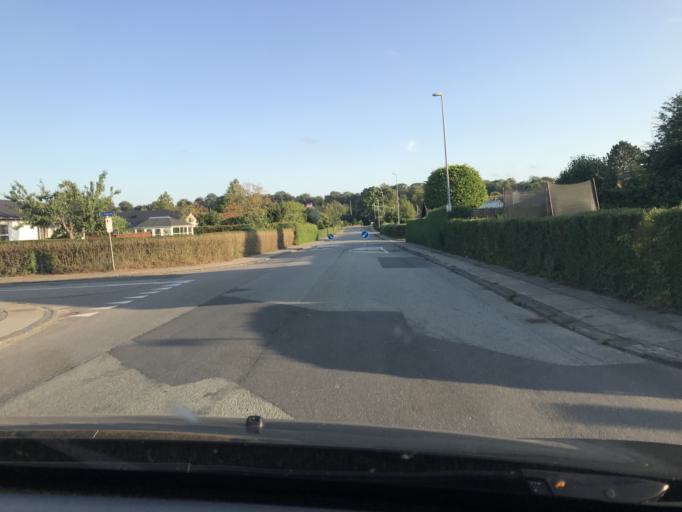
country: DK
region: South Denmark
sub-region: Vejle Kommune
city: Vejle
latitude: 55.7182
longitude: 9.5710
